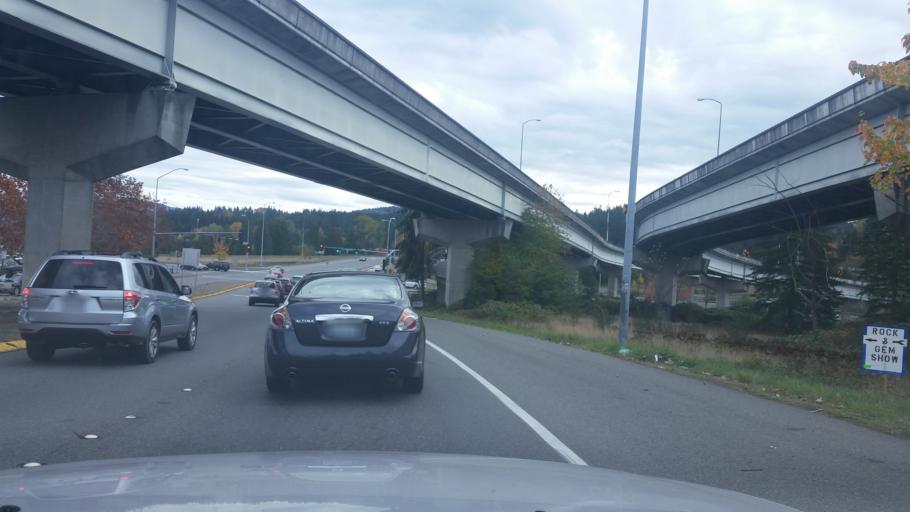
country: US
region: Washington
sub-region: King County
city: Eastgate
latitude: 47.5816
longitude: -122.1425
